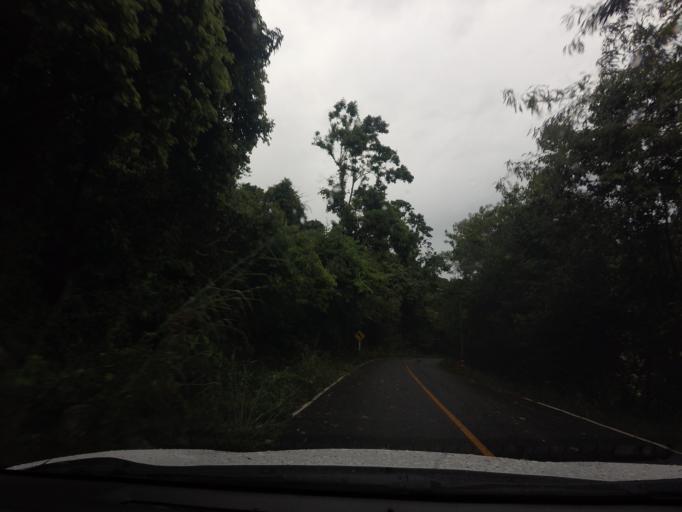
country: TH
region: Chon Buri
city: Sattahip
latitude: 12.7653
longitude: 100.9505
